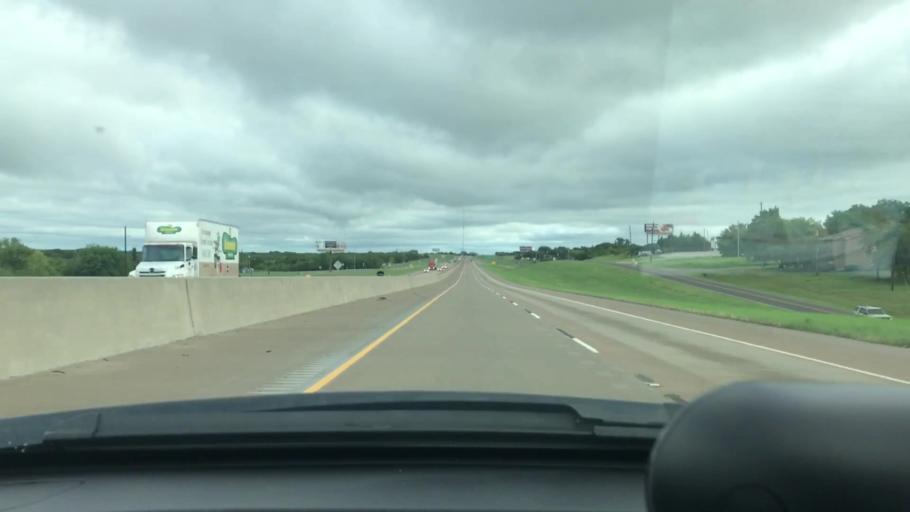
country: US
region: Texas
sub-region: Grayson County
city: Howe
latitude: 33.5082
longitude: -96.6177
